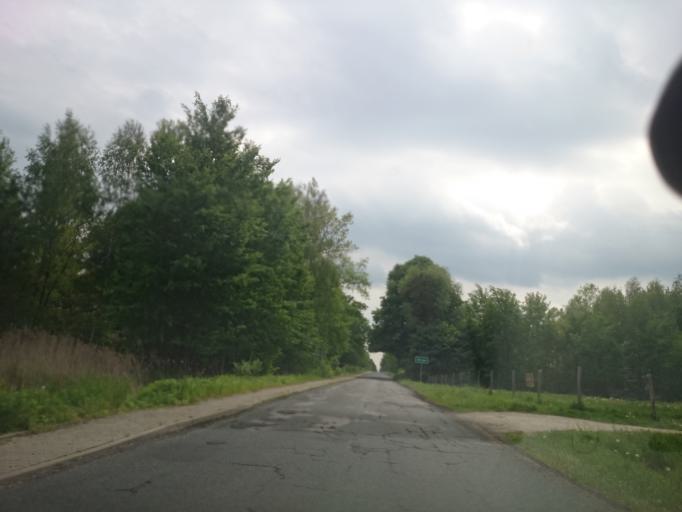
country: PL
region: Lower Silesian Voivodeship
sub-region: Powiat olesnicki
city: Dobroszyce
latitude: 51.3573
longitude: 17.2811
